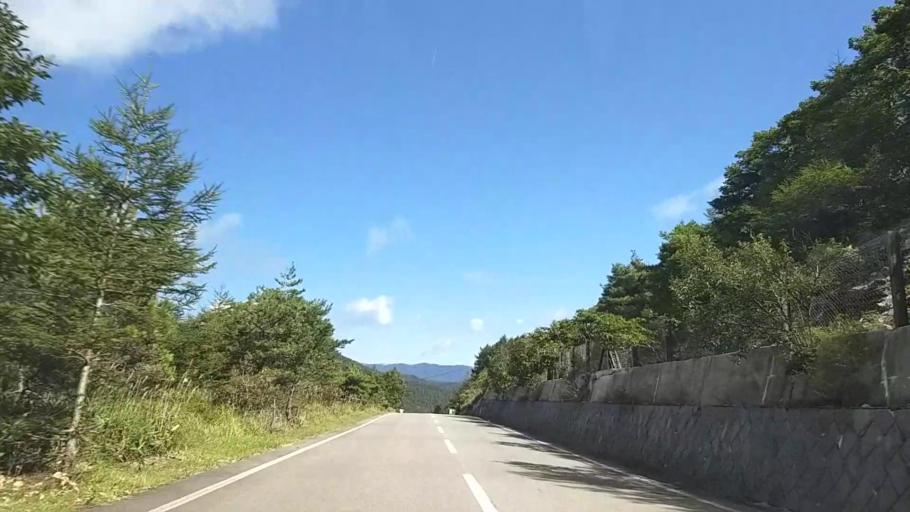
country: JP
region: Nagano
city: Suwa
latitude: 36.1434
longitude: 138.1448
